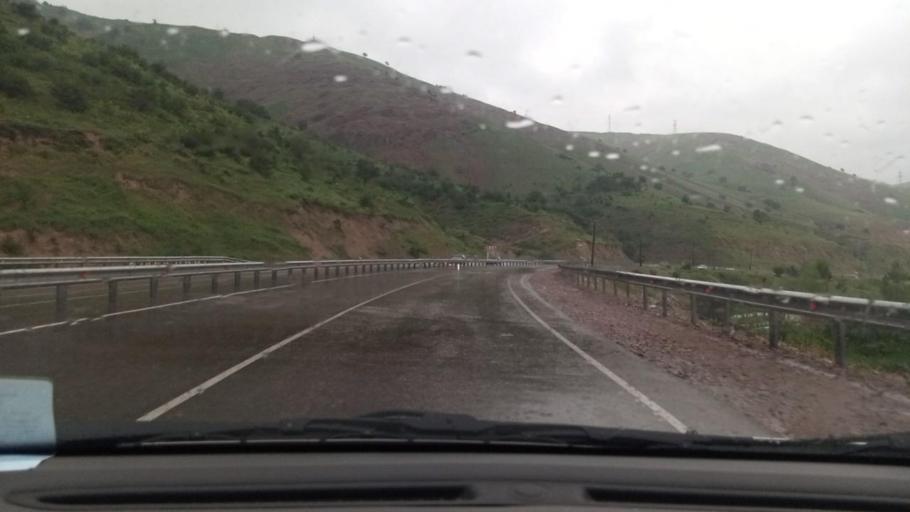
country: UZ
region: Toshkent
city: Angren
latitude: 41.0904
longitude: 70.3201
